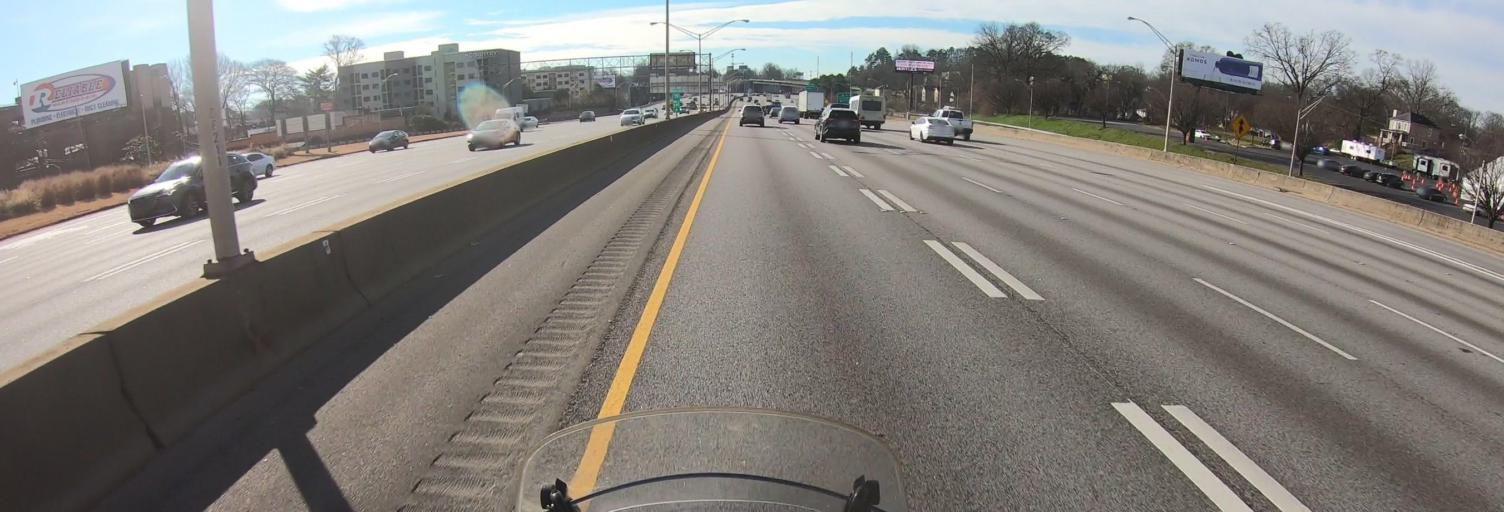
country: US
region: Georgia
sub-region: Fulton County
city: Atlanta
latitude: 33.7328
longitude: -84.3896
